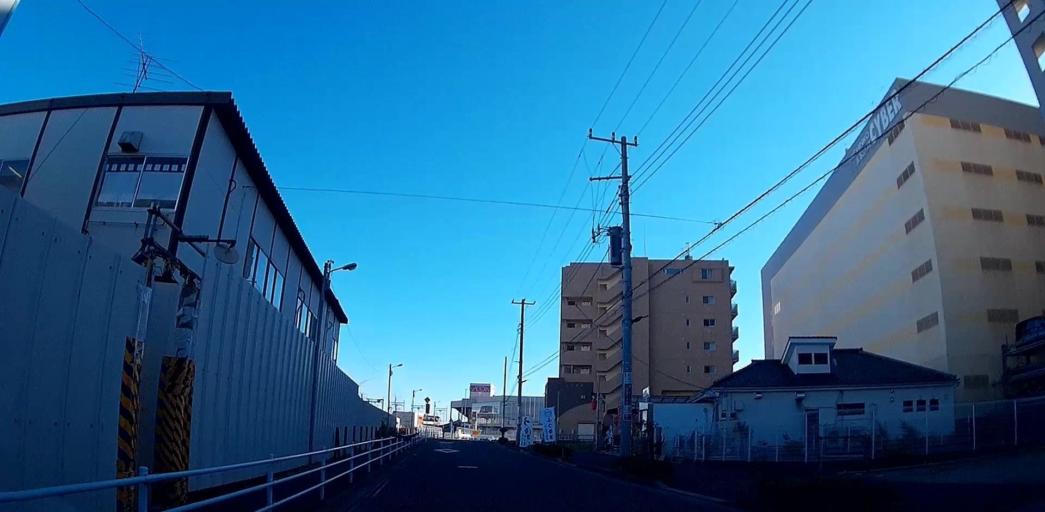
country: JP
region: Chiba
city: Shiroi
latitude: 35.7787
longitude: 139.9984
